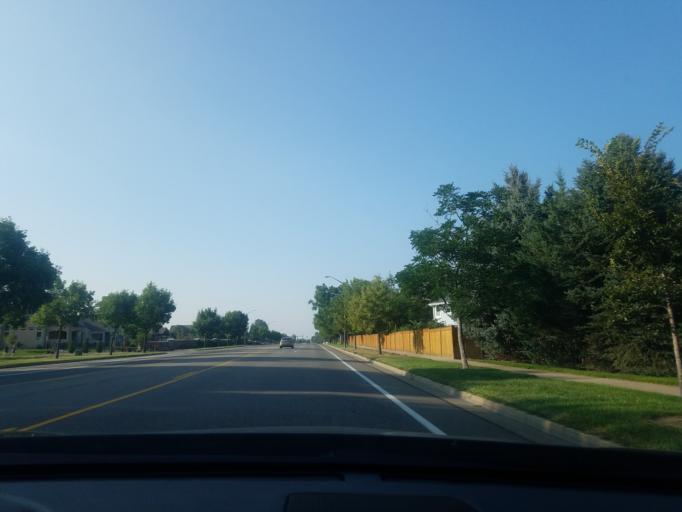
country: US
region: Colorado
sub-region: Larimer County
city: Fort Collins
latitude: 40.5170
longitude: -105.0961
